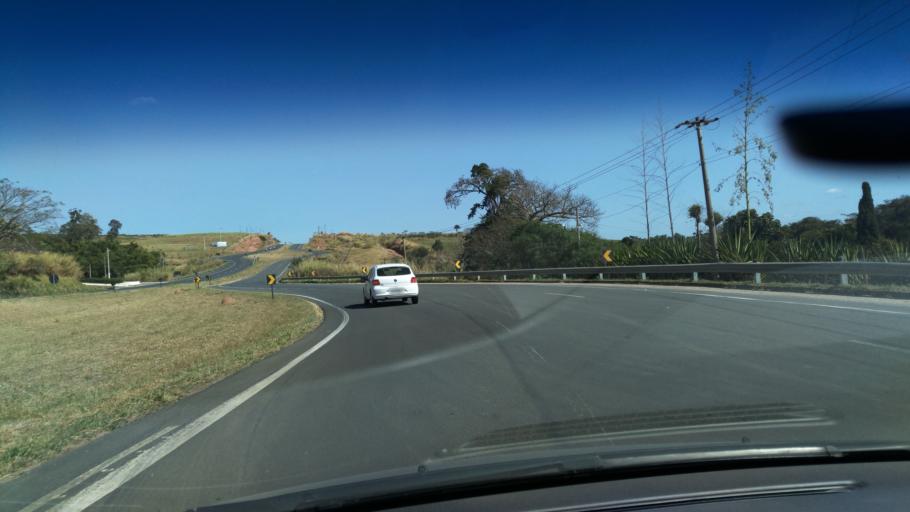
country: BR
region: Sao Paulo
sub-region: Santo Antonio Do Jardim
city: Espirito Santo do Pinhal
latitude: -22.1650
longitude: -46.7372
